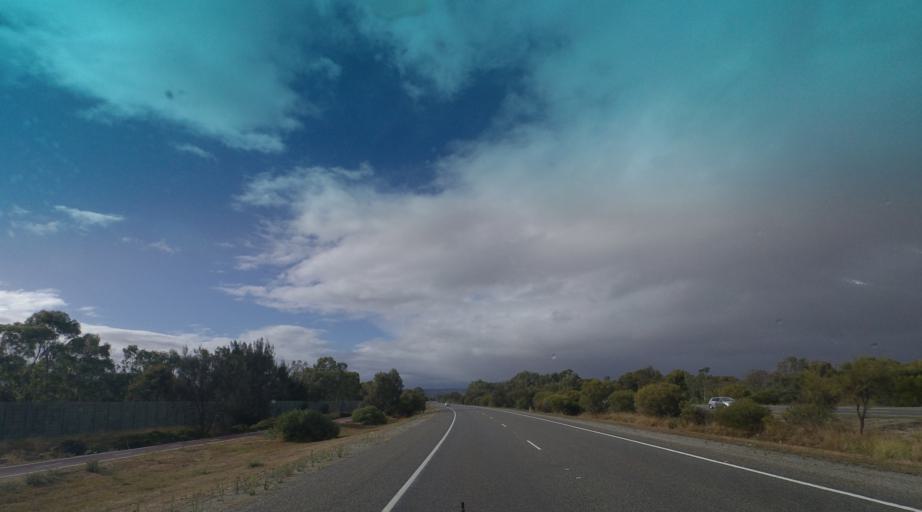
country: AU
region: Western Australia
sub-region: Serpentine-Jarrahdale
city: Oakford
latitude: -32.2013
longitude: 115.9649
